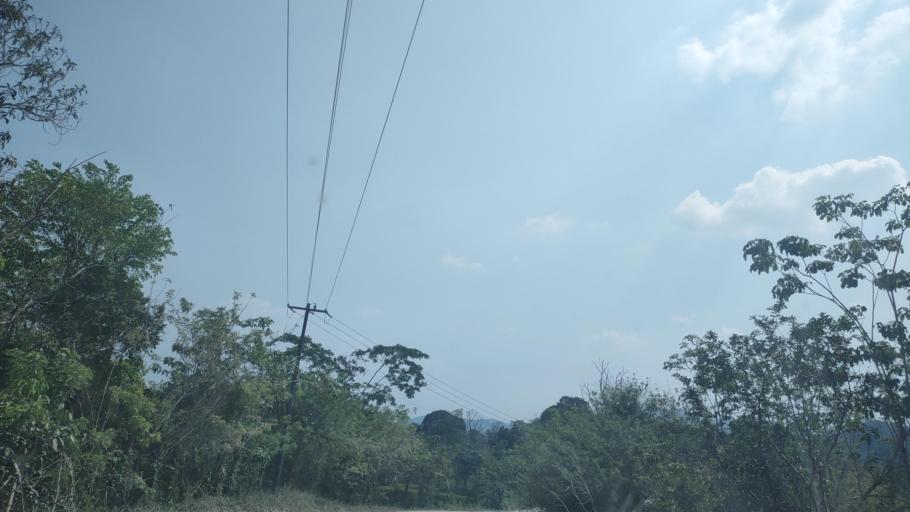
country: MX
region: Tabasco
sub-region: Huimanguillo
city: Francisco Rueda
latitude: 17.5659
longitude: -93.8865
